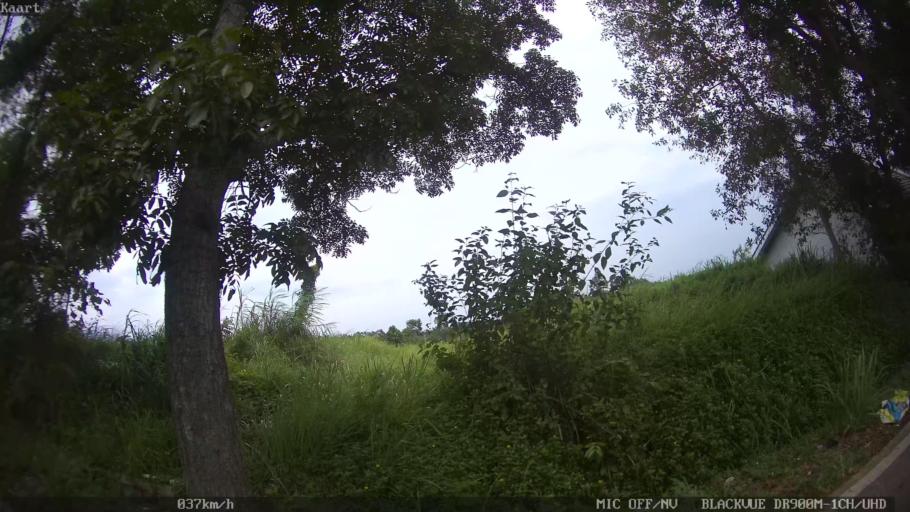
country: ID
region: Lampung
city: Kedaton
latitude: -5.3814
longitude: 105.2112
